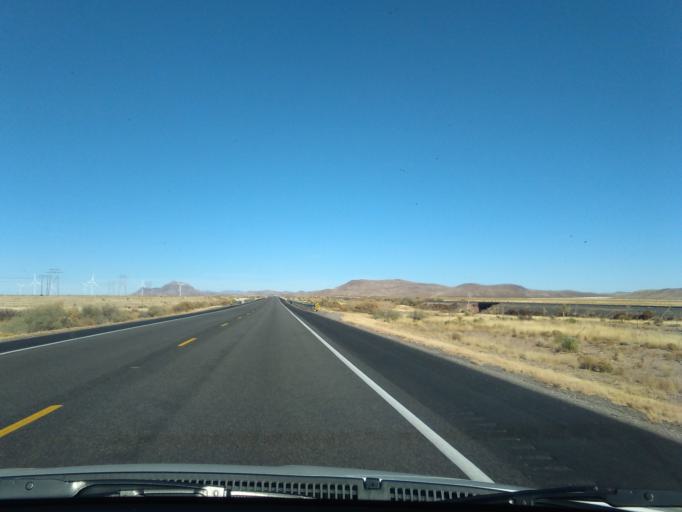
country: US
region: New Mexico
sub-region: Luna County
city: Deming
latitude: 32.4960
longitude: -107.5161
